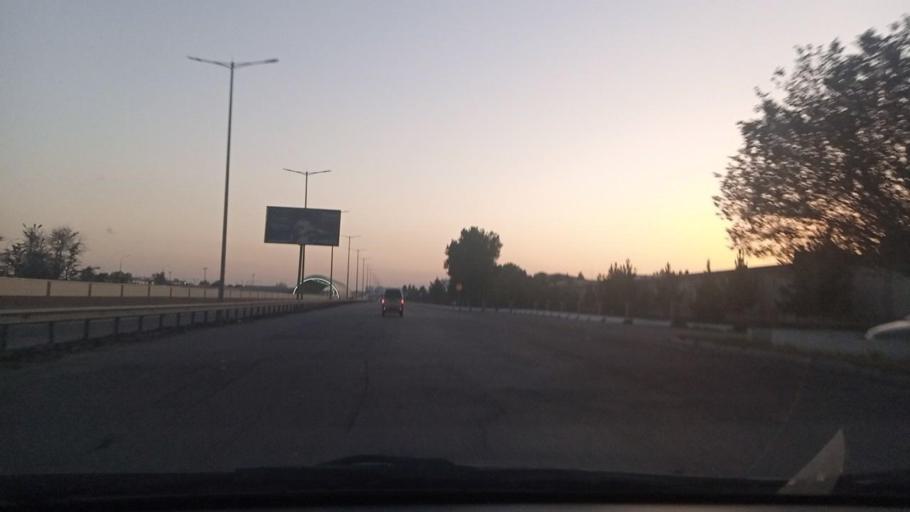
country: UZ
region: Toshkent Shahri
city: Bektemir
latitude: 41.2533
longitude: 69.3570
